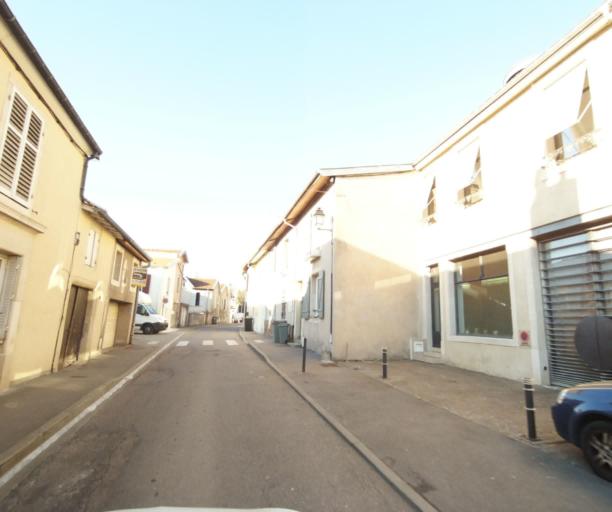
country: FR
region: Lorraine
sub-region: Departement de Meurthe-et-Moselle
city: Malzeville
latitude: 48.7104
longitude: 6.1871
